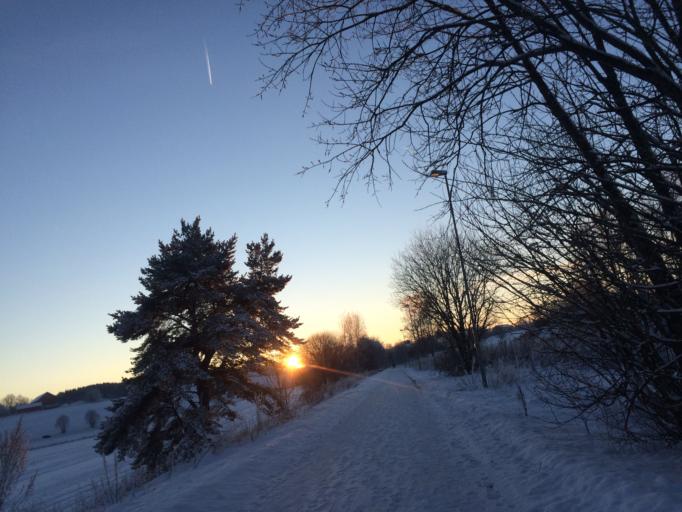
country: NO
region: Akershus
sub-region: Ski
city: Ski
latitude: 59.6910
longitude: 10.8209
